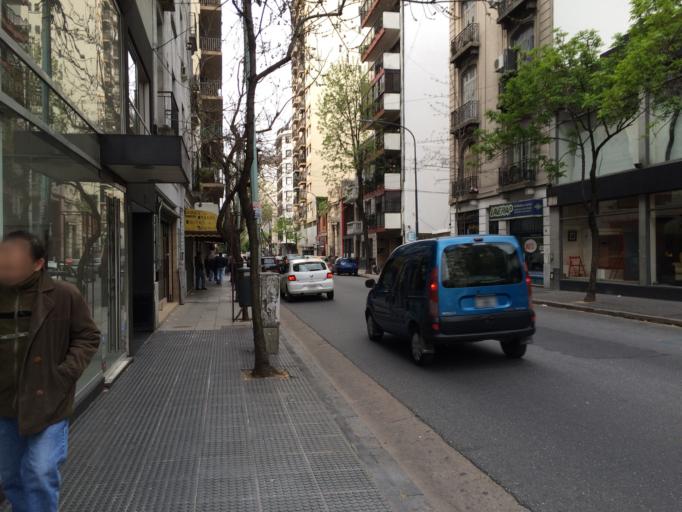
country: AR
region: Buenos Aires F.D.
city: Buenos Aires
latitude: -34.6143
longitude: -58.4014
